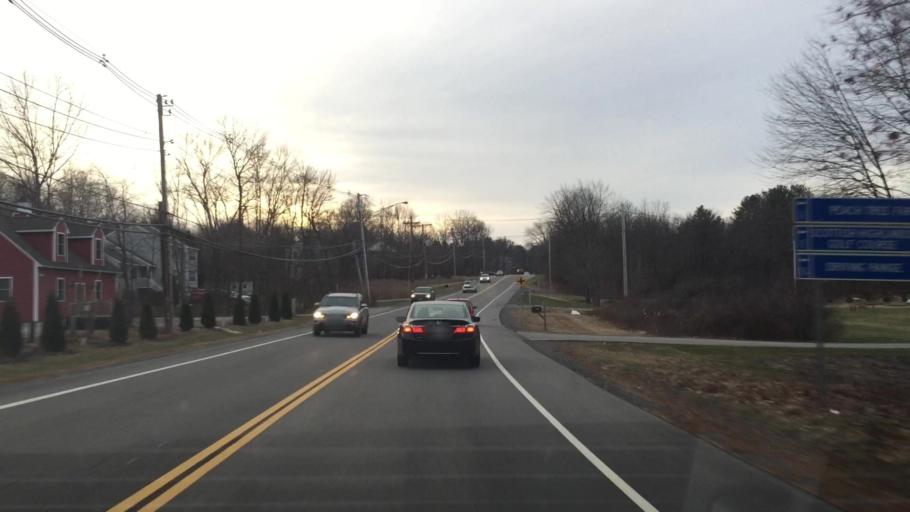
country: US
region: New Hampshire
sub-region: Rockingham County
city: Salem
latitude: 42.7619
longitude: -71.2539
